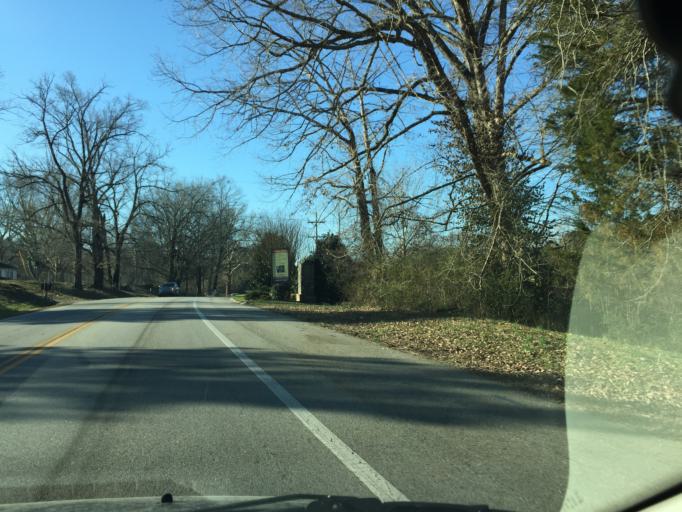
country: US
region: Tennessee
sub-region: Hamilton County
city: Collegedale
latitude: 35.0549
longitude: -85.0694
